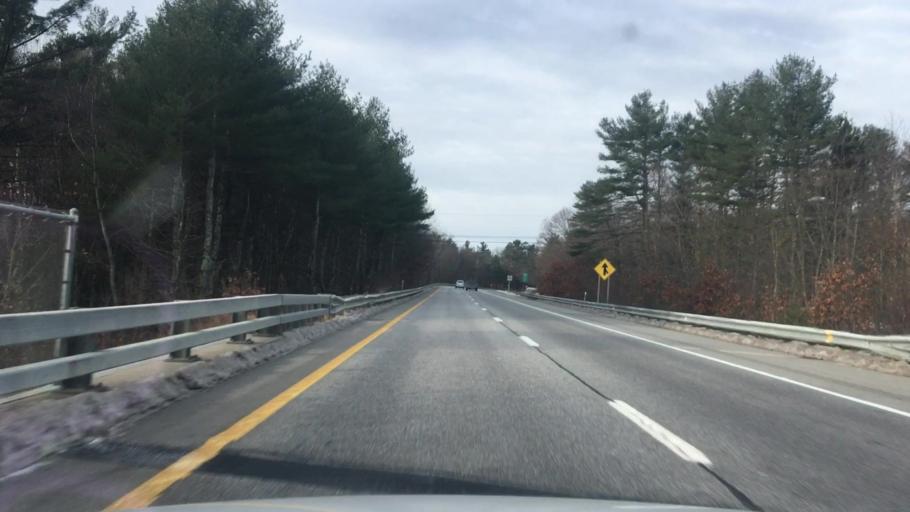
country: US
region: New Hampshire
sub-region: Merrimack County
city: Hopkinton
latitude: 43.1819
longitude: -71.6884
